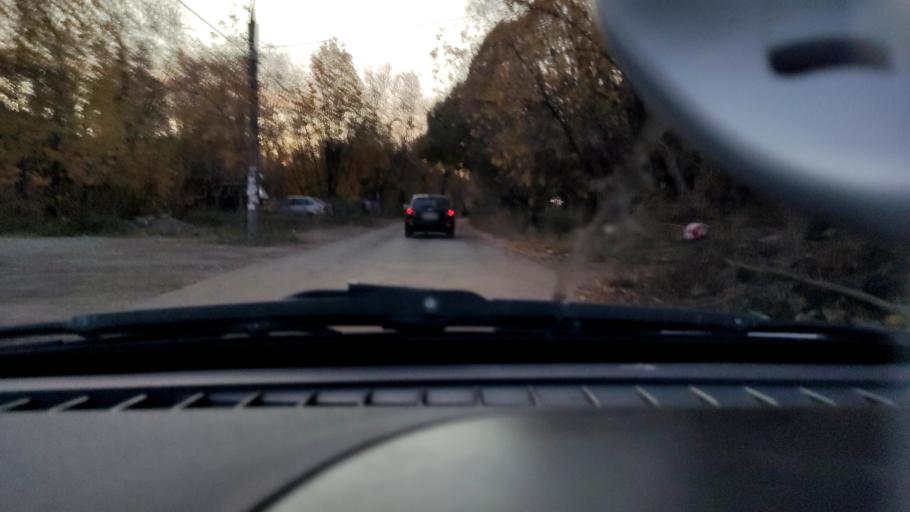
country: RU
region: Perm
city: Perm
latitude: 57.9612
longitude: 56.2351
